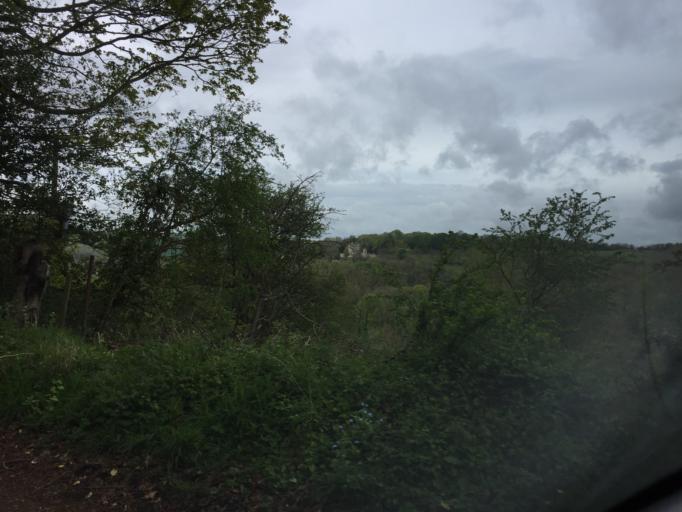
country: GB
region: England
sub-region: Bath and North East Somerset
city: Bath
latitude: 51.3568
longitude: -2.3398
